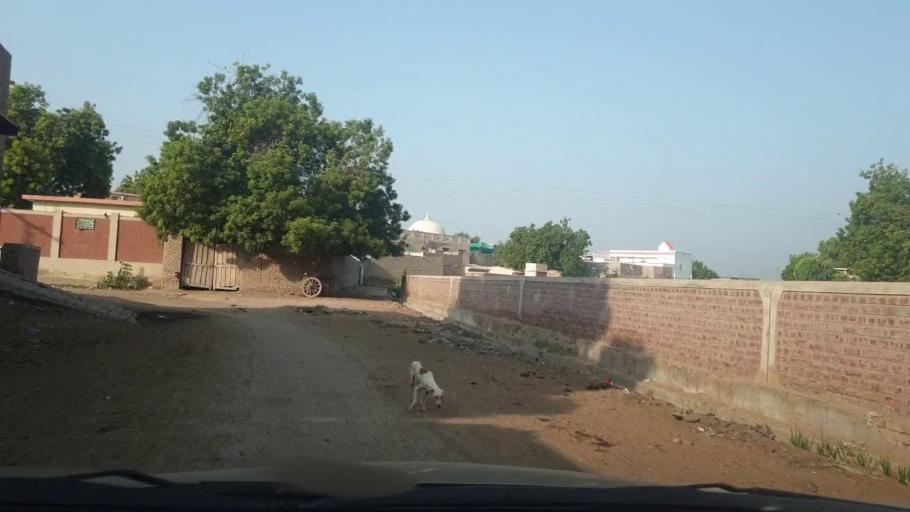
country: PK
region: Sindh
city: Larkana
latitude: 27.5804
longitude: 68.1775
